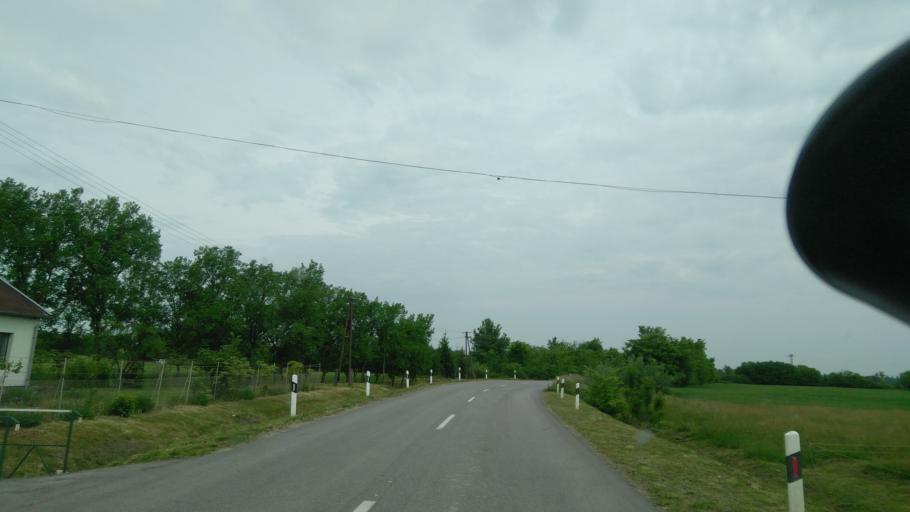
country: HU
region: Bekes
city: Szeghalom
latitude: 46.9912
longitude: 21.1793
